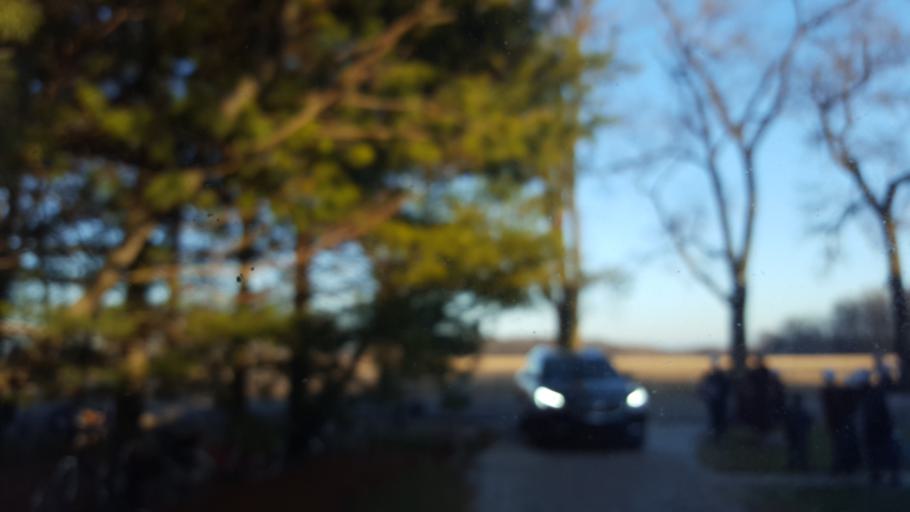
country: US
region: Indiana
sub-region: Elkhart County
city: Nappanee
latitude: 41.4512
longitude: -86.0209
